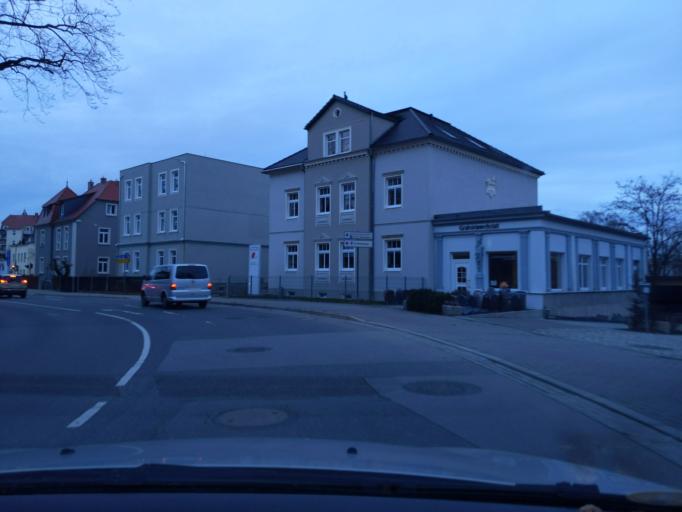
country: DE
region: Saxony
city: Bautzen
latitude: 51.1833
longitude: 14.4358
